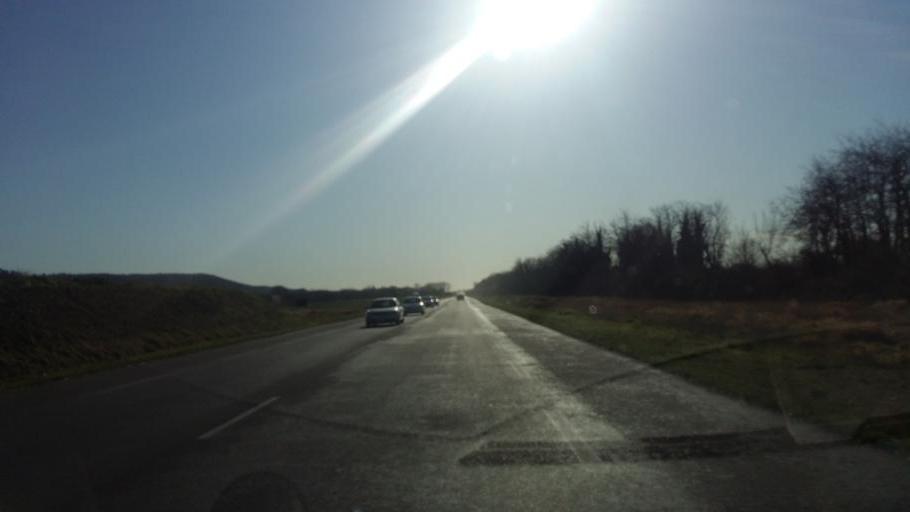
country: FR
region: Provence-Alpes-Cote d'Azur
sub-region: Departement du Vaucluse
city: Villelaure
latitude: 43.6995
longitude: 5.4138
